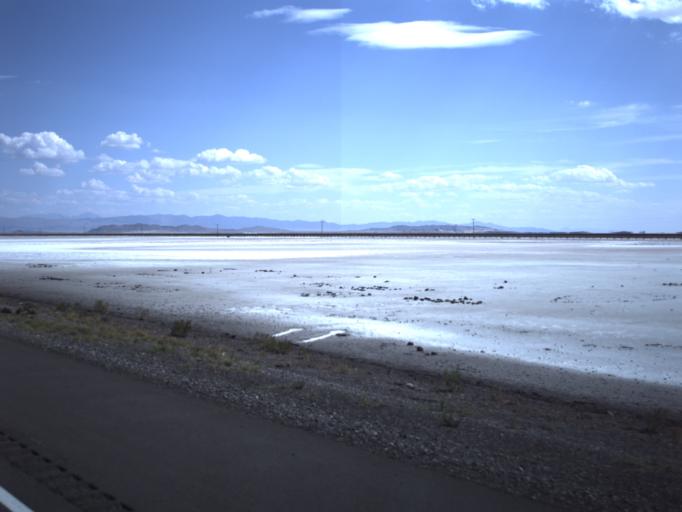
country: US
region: Utah
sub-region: Tooele County
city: Wendover
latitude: 40.7294
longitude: -113.4353
